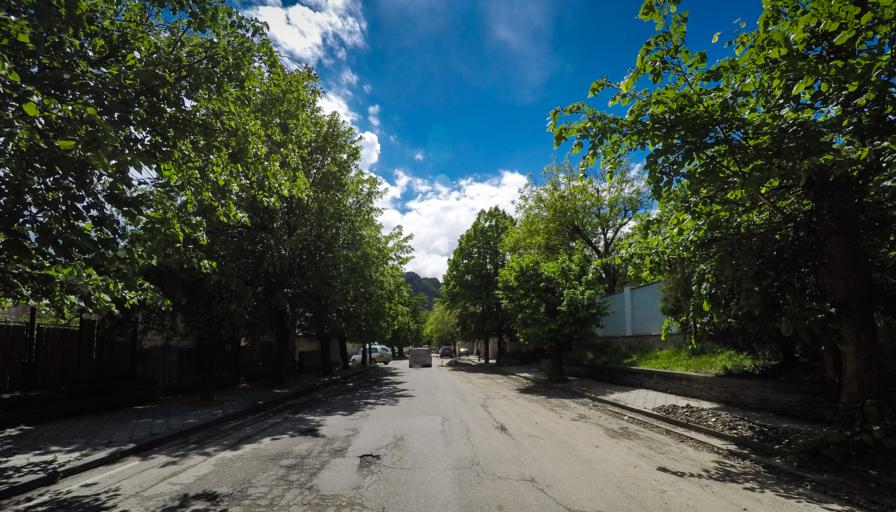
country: GE
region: Mtskheta-Mtianeti
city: Mtskheta
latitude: 41.8431
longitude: 44.7177
